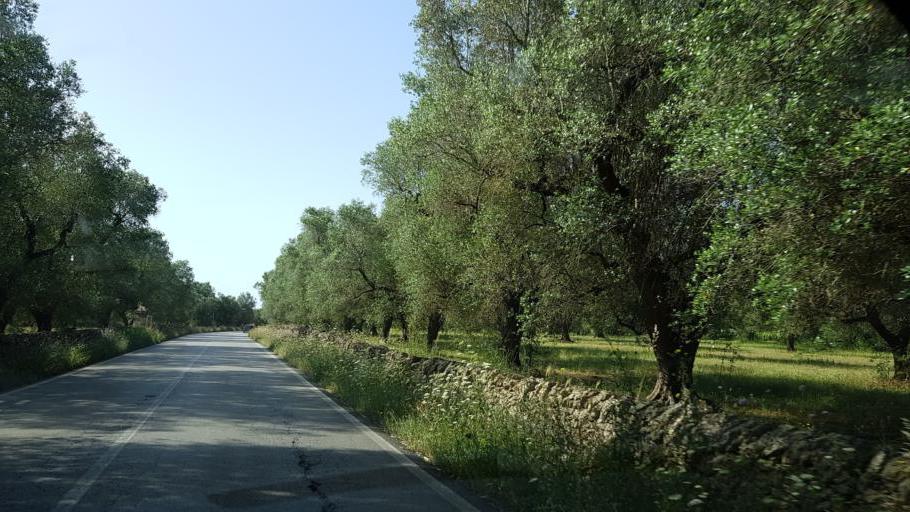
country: IT
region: Apulia
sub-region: Provincia di Brindisi
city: Mesagne
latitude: 40.5180
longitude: 17.8248
